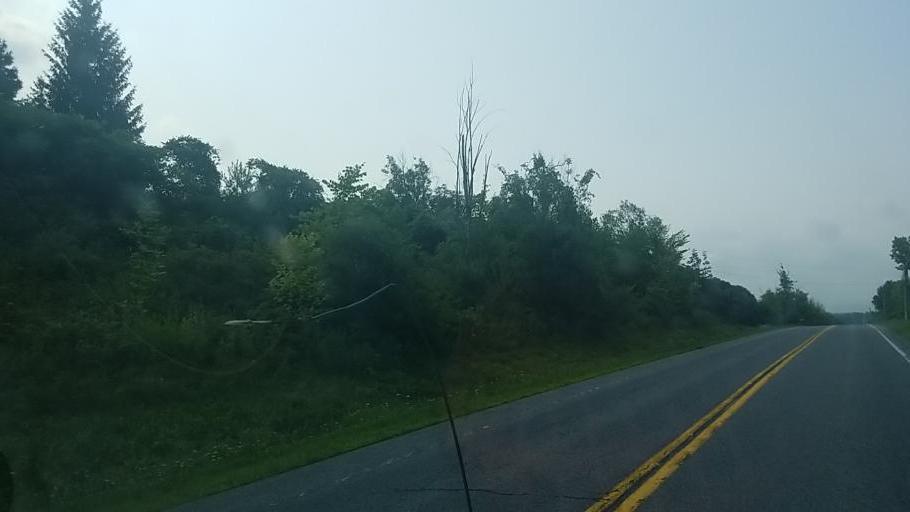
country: US
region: New York
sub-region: Fulton County
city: Johnstown
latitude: 43.0086
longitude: -74.4059
